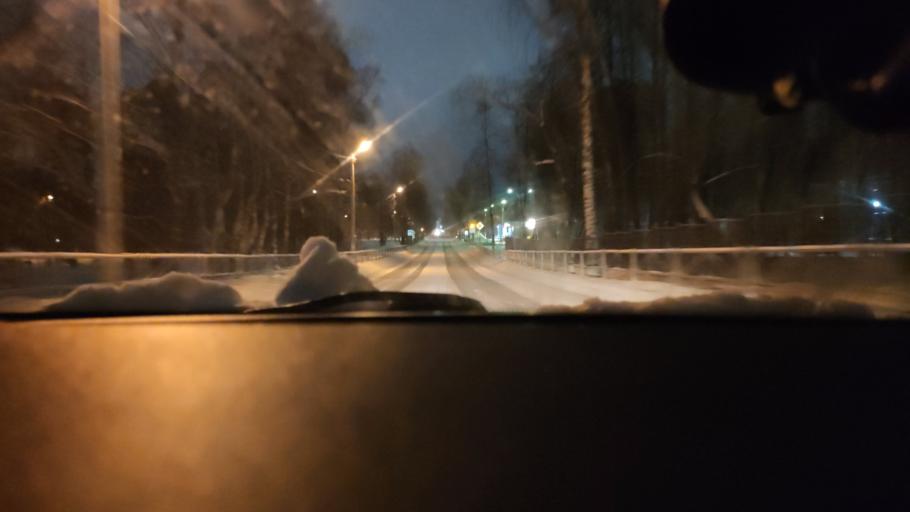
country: RU
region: Perm
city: Krasnokamsk
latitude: 58.0836
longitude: 55.7461
